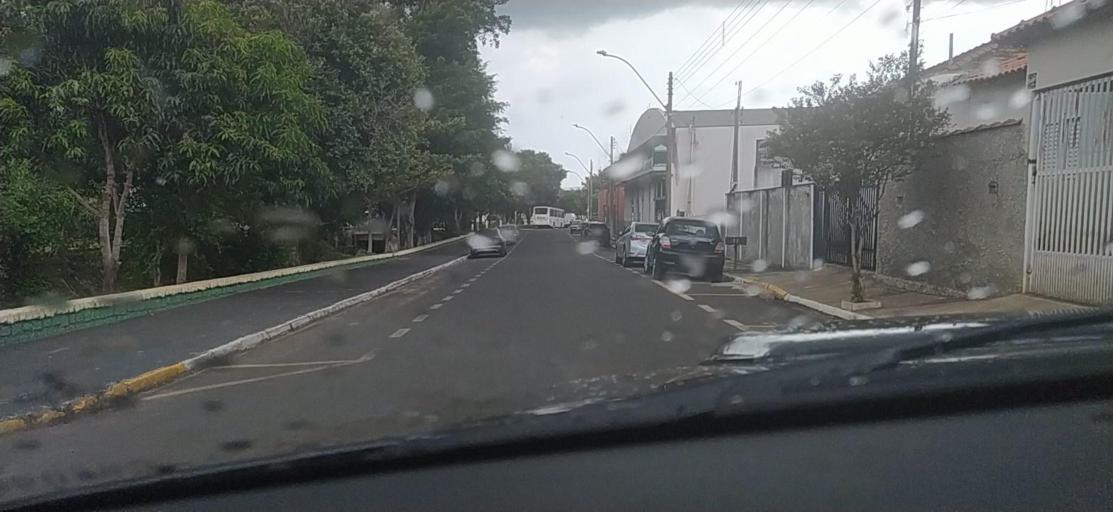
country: BR
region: Sao Paulo
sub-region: Pindorama
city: Pindorama
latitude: -21.1859
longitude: -48.9040
